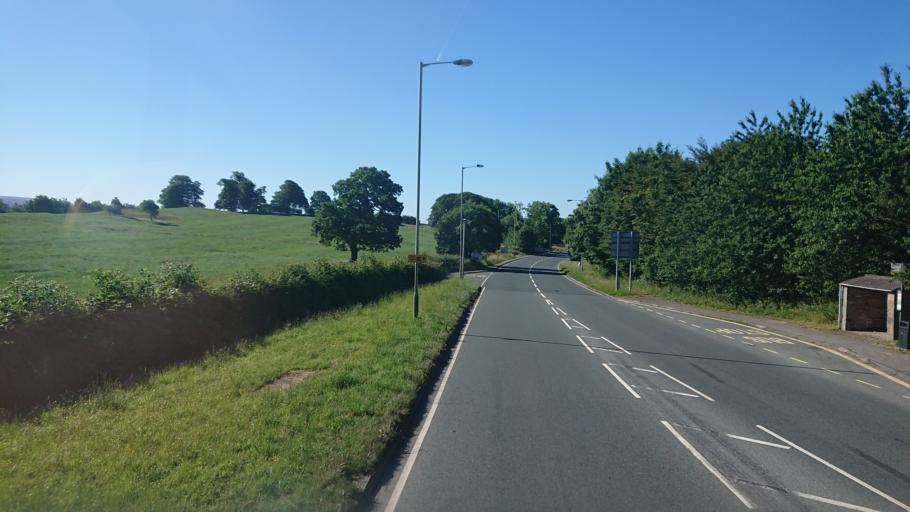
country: GB
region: England
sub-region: Lancashire
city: Galgate
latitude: 53.9805
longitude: -2.7852
